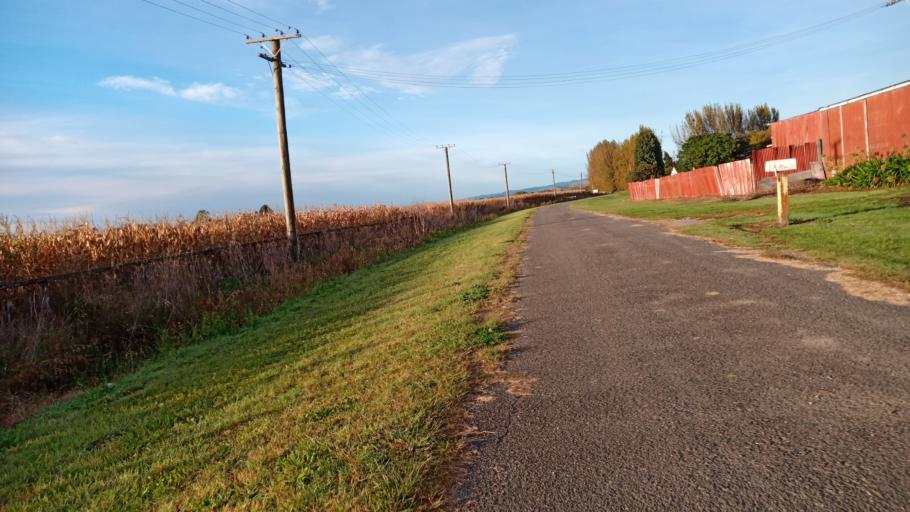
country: NZ
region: Gisborne
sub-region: Gisborne District
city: Gisborne
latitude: -38.6522
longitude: 177.9423
